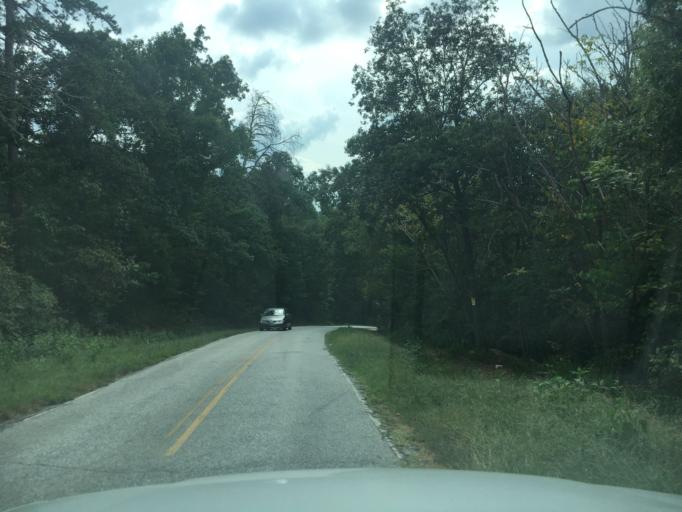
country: US
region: South Carolina
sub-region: Spartanburg County
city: Duncan
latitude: 34.9247
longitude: -82.1269
